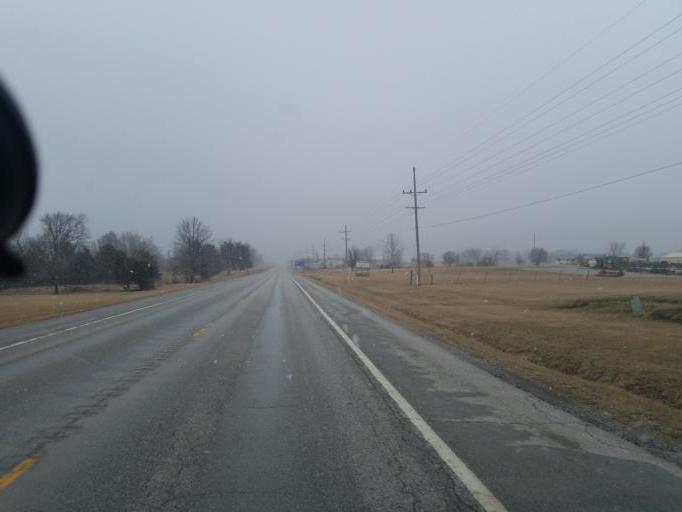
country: US
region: Missouri
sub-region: Adair County
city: Kirksville
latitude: 40.2559
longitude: -92.5826
